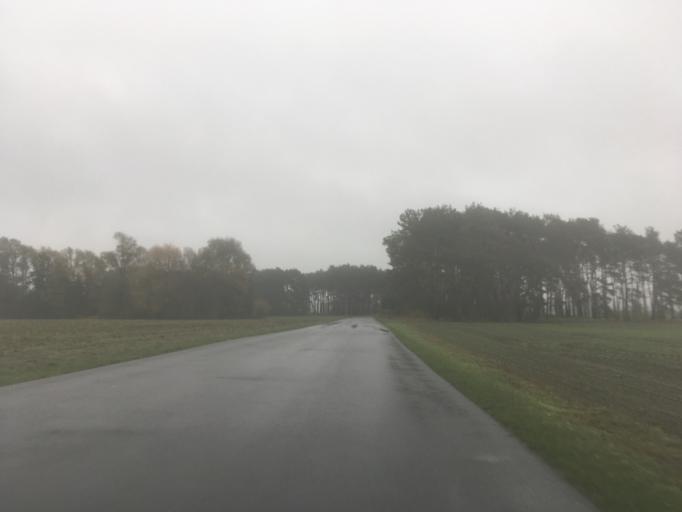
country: DE
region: Brandenburg
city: Schlepzig
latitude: 52.0150
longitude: 13.9479
